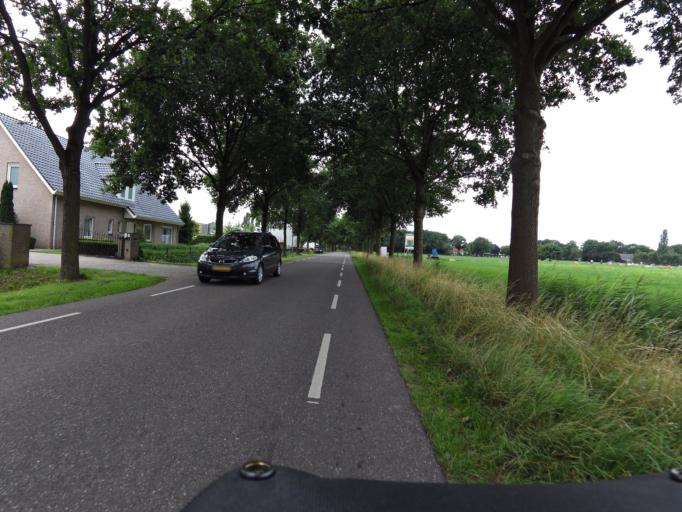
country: NL
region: North Brabant
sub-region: Gemeente Breda
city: Breda
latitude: 51.5645
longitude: 4.7005
